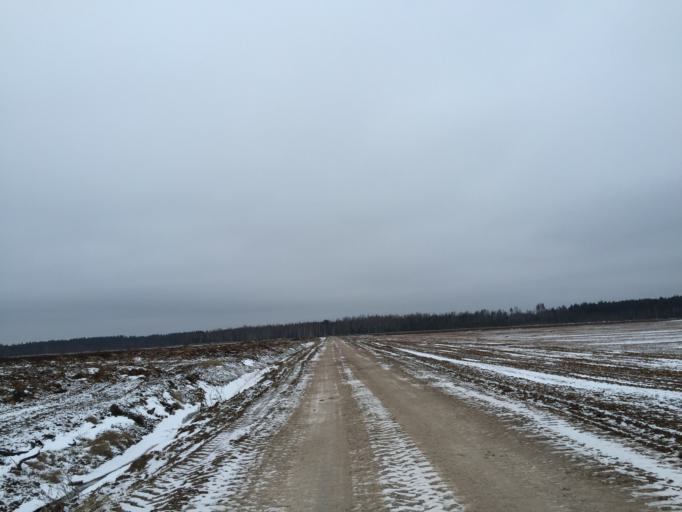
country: LV
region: Saulkrastu
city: Saulkrasti
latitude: 57.2395
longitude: 24.4999
